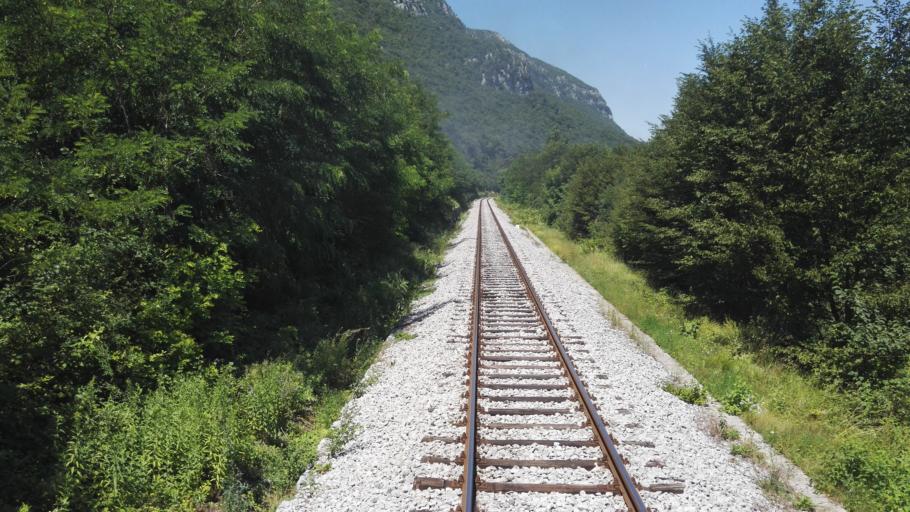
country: SI
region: Nova Gorica
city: Solkan
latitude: 45.9883
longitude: 13.6480
